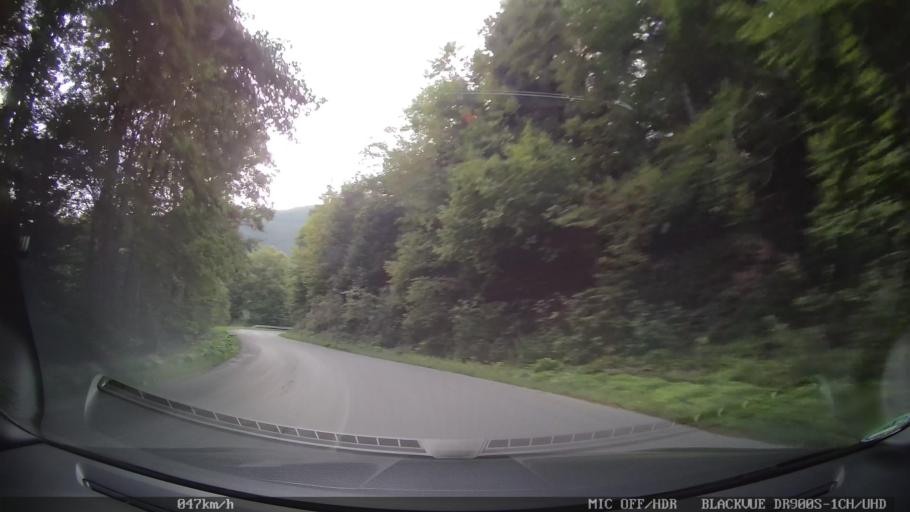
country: HR
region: Primorsko-Goranska
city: Vrbovsko
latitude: 45.2016
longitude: 15.0155
